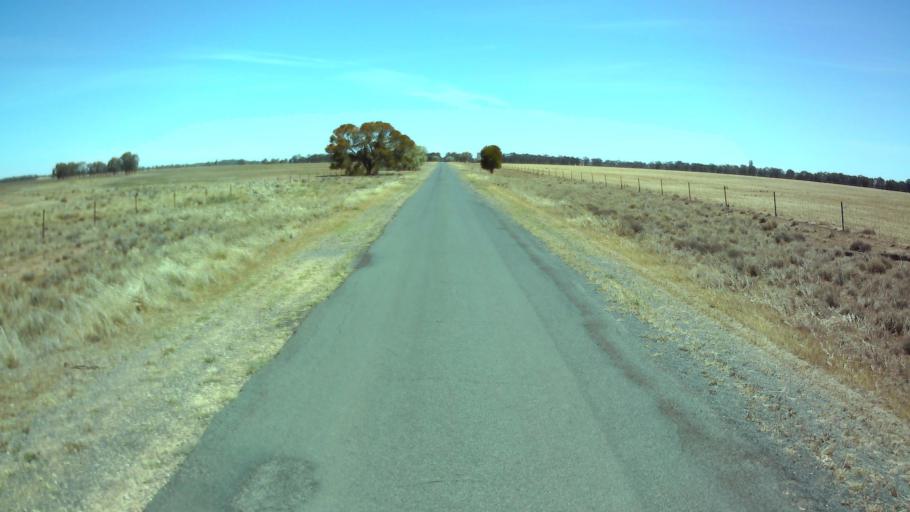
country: AU
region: New South Wales
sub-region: Weddin
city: Grenfell
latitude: -33.8548
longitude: 147.6950
